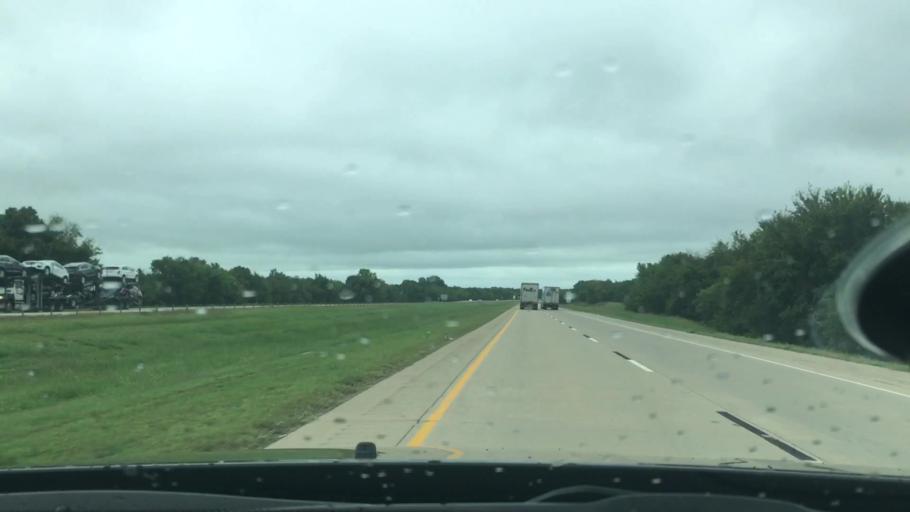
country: US
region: Oklahoma
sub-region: McIntosh County
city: Checotah
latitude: 35.4564
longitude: -95.6368
